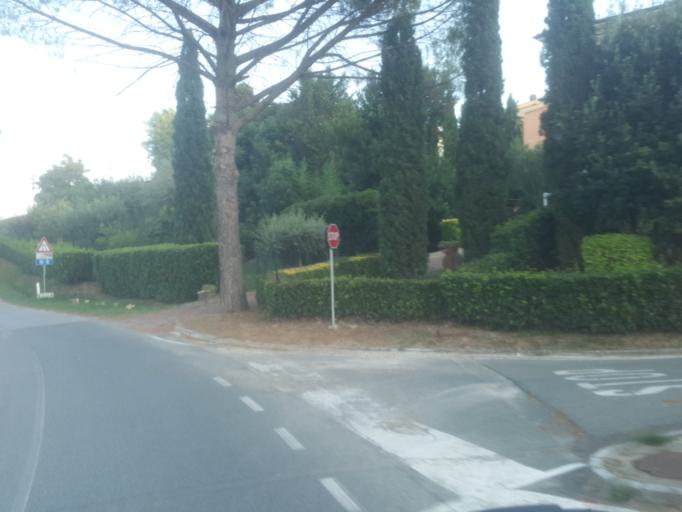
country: IT
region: Tuscany
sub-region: Province of Florence
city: Certaldo
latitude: 43.5391
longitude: 11.0333
